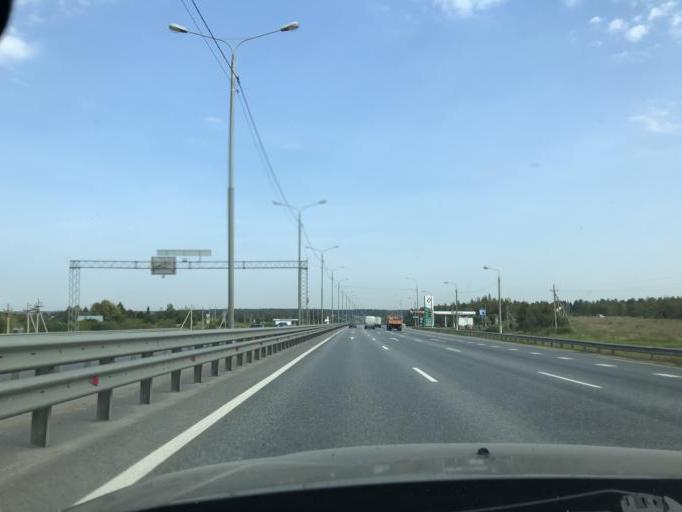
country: RU
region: Moskovskaya
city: Novyy Byt
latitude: 55.0692
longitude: 37.5687
